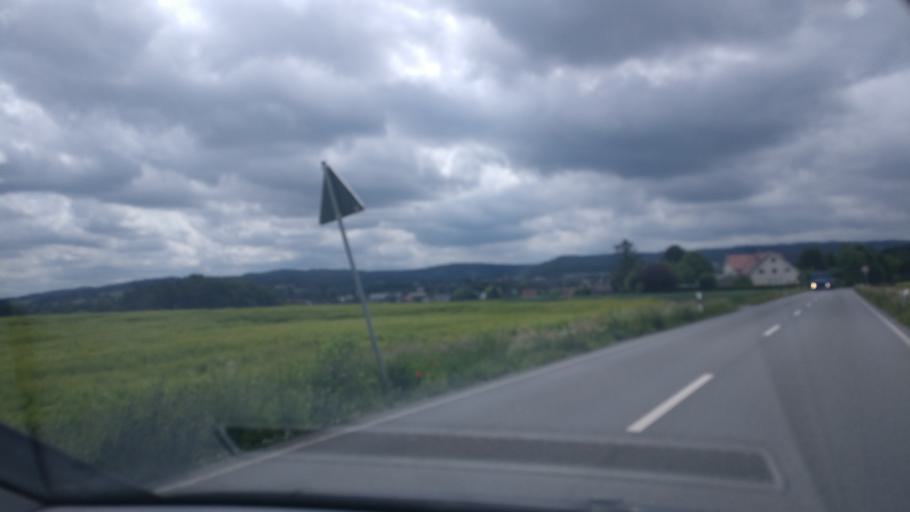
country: DE
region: North Rhine-Westphalia
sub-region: Regierungsbezirk Detmold
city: Leopoldshohe
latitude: 51.9890
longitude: 8.7200
